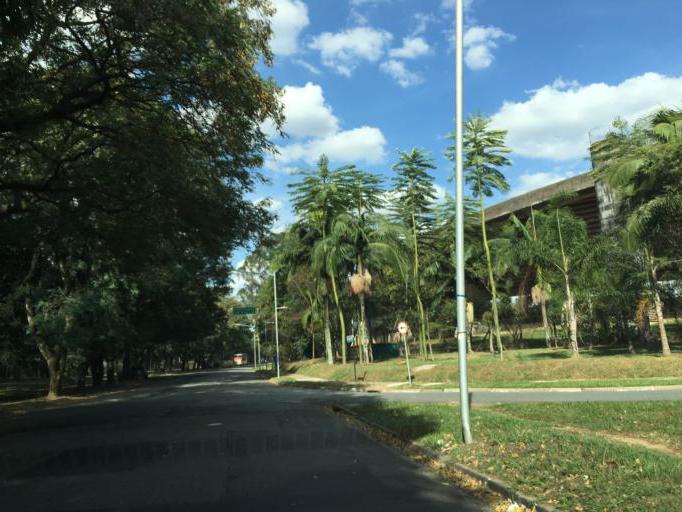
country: BR
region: Sao Paulo
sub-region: Osasco
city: Osasco
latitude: -23.5577
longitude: -46.7191
